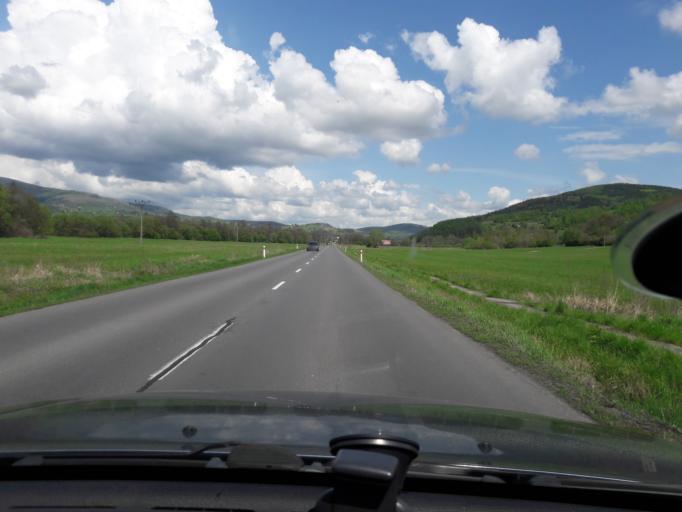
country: SK
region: Banskobystricky
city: Detva
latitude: 48.5500
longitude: 19.4699
